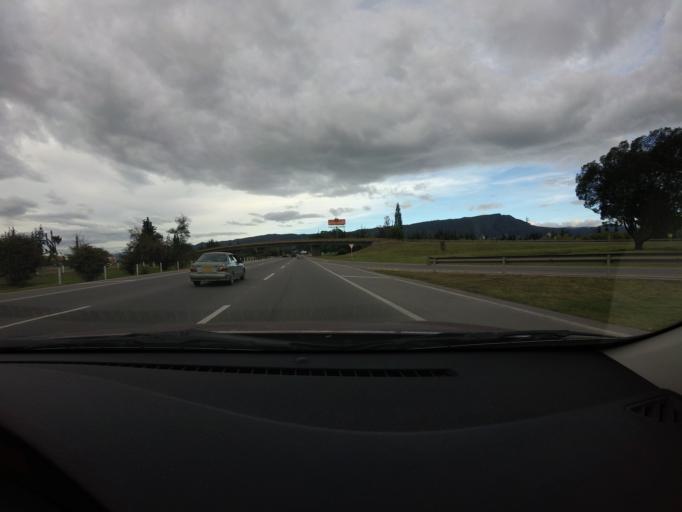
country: CO
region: Cundinamarca
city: Sopo
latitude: 4.9391
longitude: -73.9672
